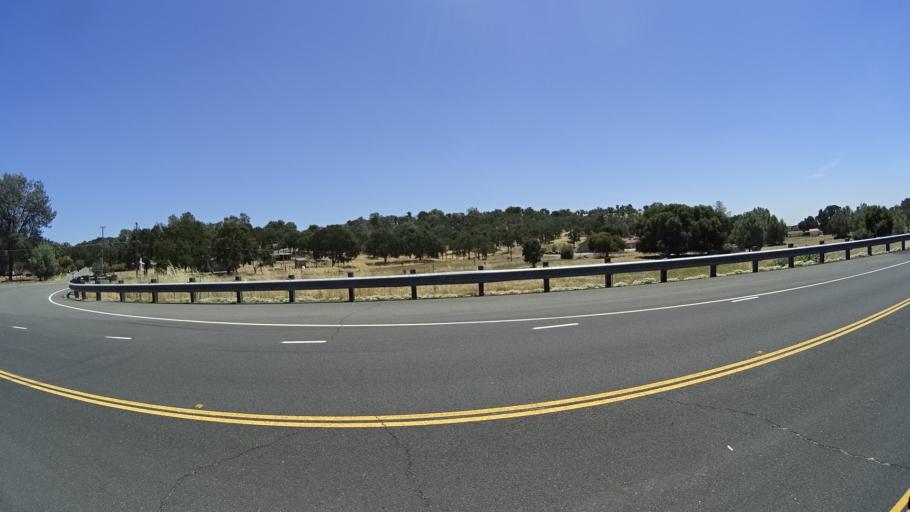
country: US
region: California
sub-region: Calaveras County
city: Rancho Calaveras
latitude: 38.1227
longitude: -120.8779
